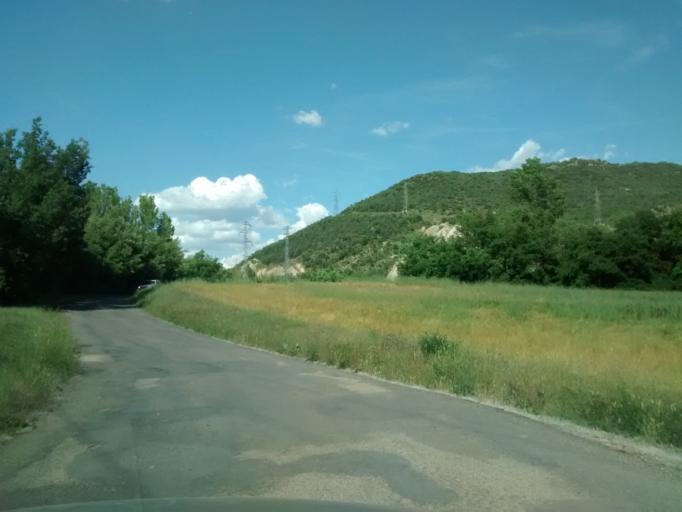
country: ES
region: Aragon
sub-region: Provincia de Huesca
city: Sabinanigo
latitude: 42.4898
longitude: -0.3728
